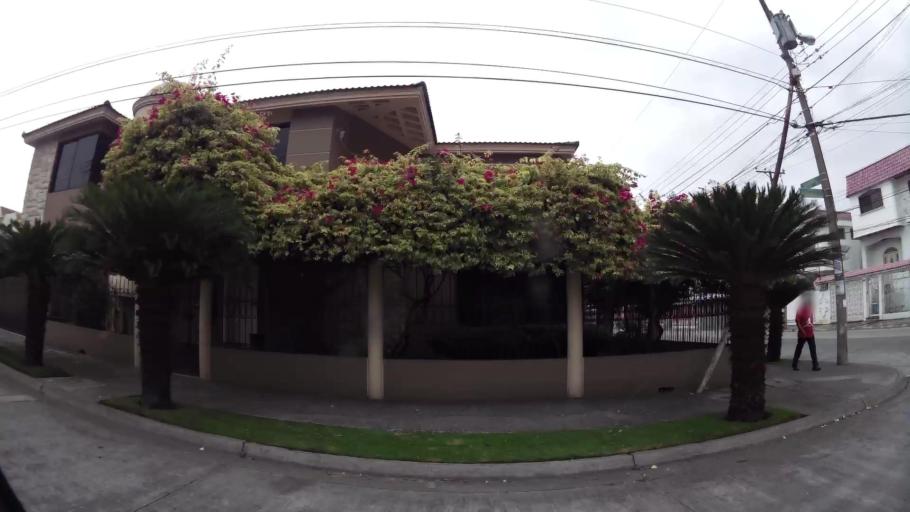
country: EC
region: Guayas
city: Eloy Alfaro
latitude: -2.1480
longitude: -79.8898
